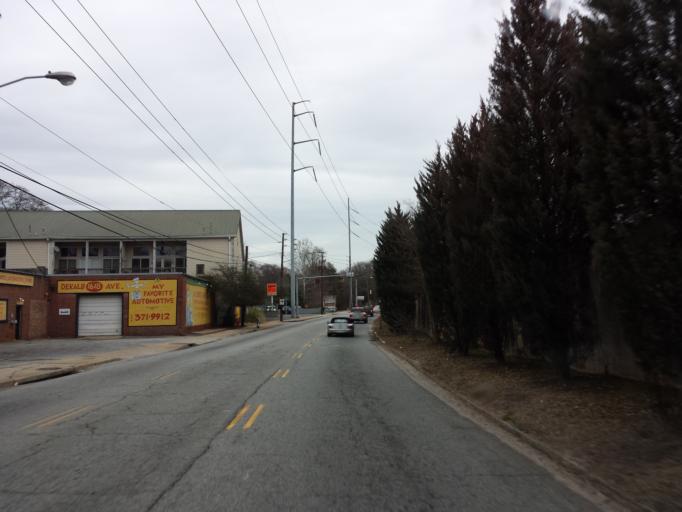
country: US
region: Georgia
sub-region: DeKalb County
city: Druid Hills
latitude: 33.7626
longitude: -84.3349
